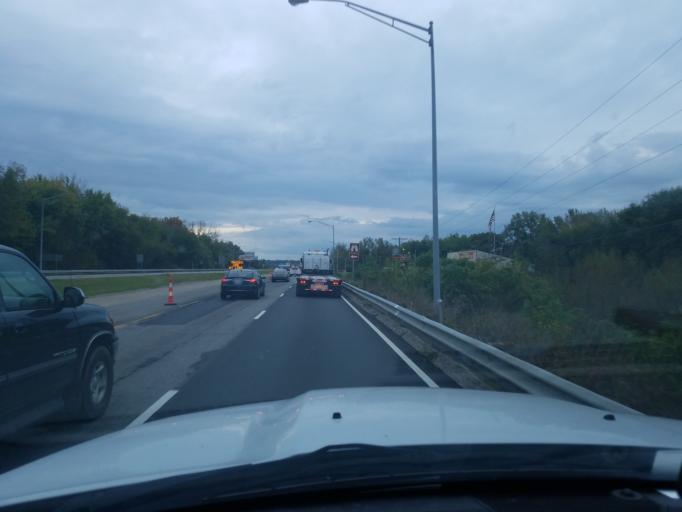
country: US
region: Indiana
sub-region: Vanderburgh County
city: Evansville
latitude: 37.9273
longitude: -87.5484
